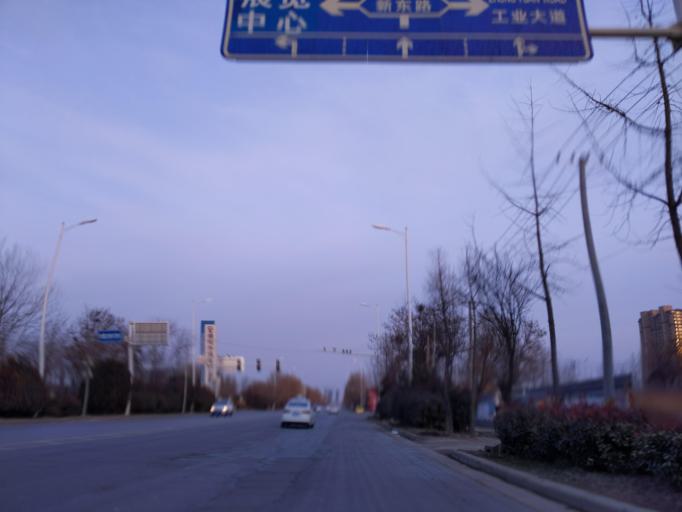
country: CN
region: Henan Sheng
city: Zhongyuanlu
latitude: 35.7867
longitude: 115.1263
